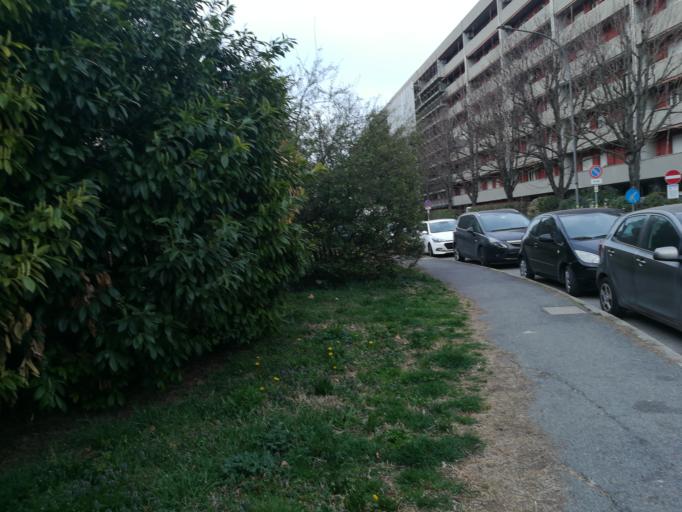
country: IT
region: Emilia-Romagna
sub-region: Provincia di Bologna
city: Progresso
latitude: 44.5467
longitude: 11.3609
